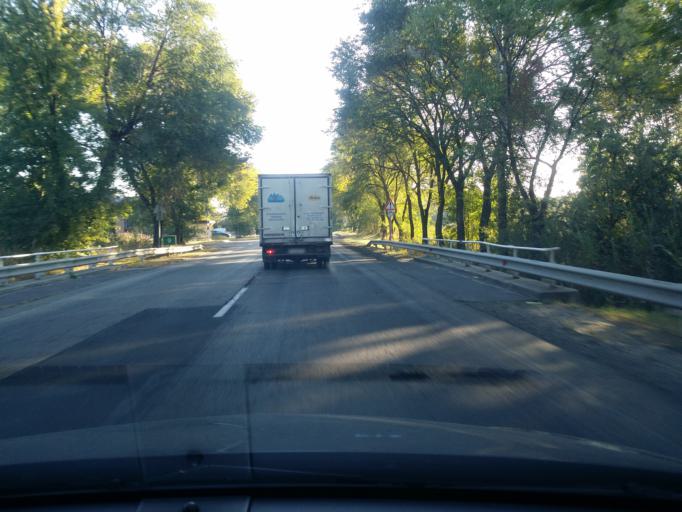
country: HU
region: Bacs-Kiskun
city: Kecskemet
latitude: 46.9147
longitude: 19.7912
